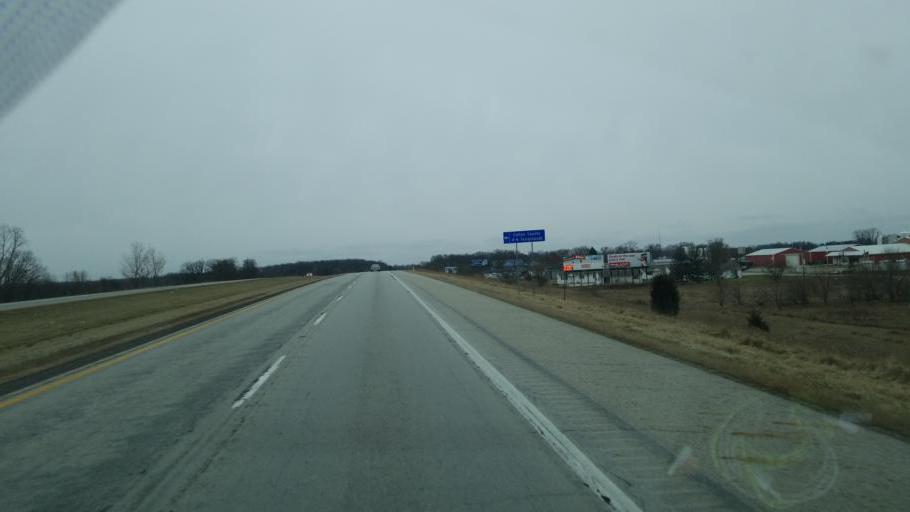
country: US
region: Indiana
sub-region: Fulton County
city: Rochester
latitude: 41.0804
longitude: -86.2408
